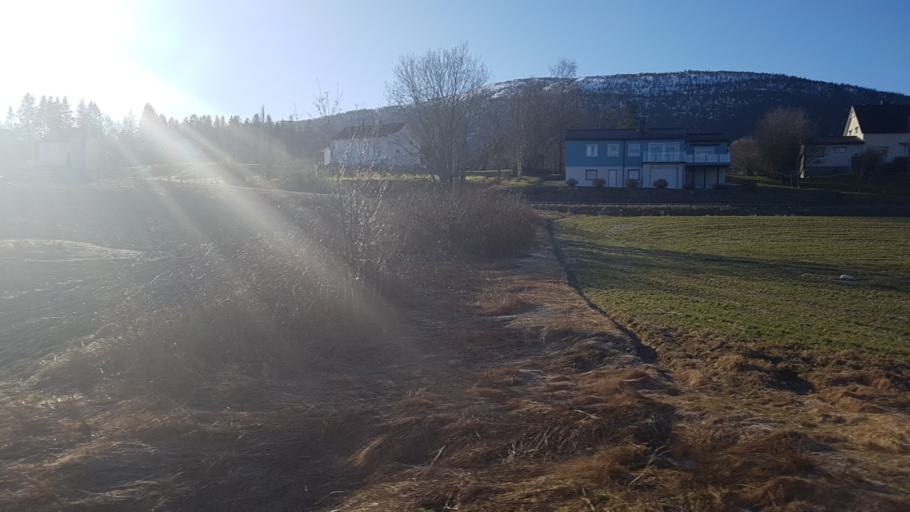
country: NO
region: Nord-Trondelag
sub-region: Levanger
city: Skogn
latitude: 63.6176
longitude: 11.0559
